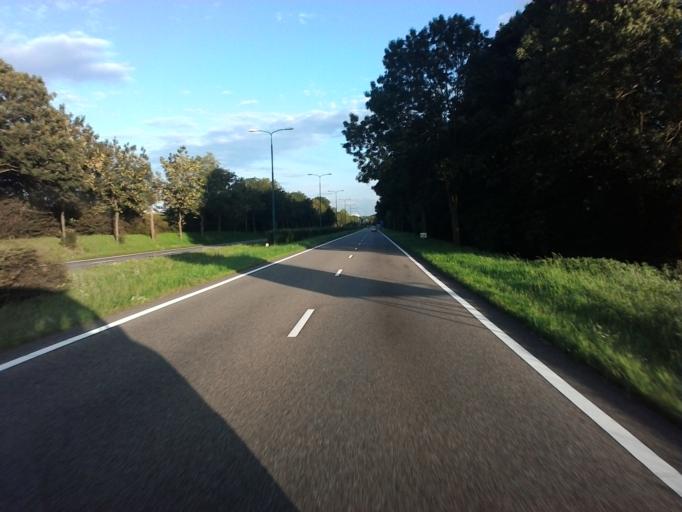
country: NL
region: Utrecht
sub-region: Stichtse Vecht
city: Maarssen
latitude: 52.1344
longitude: 5.0855
